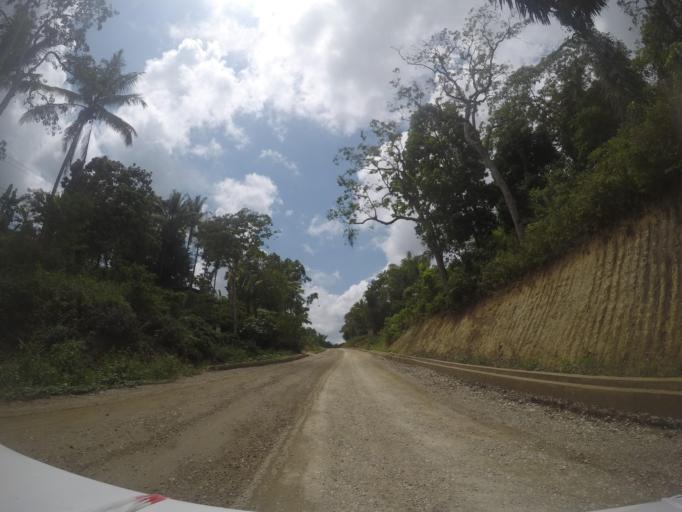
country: TL
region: Baucau
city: Venilale
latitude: -8.5801
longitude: 126.3897
